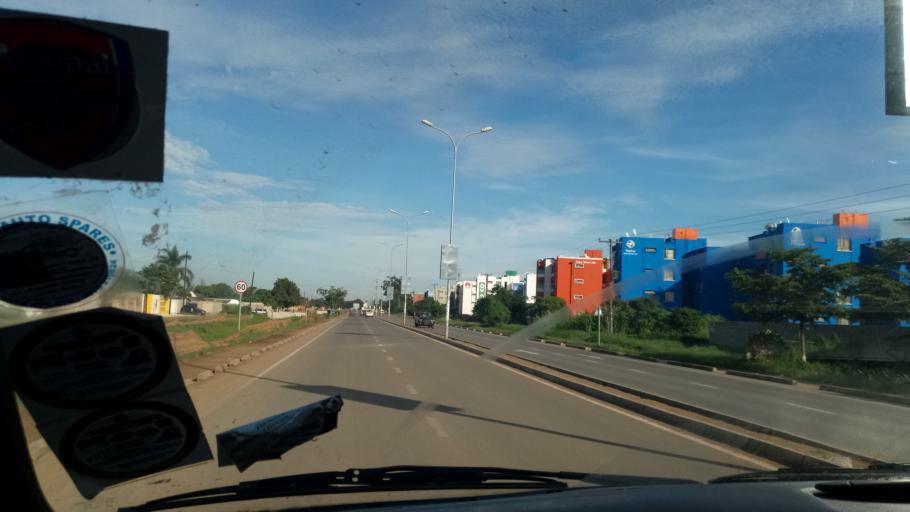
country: ZM
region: Lusaka
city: Lusaka
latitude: -15.4375
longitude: 28.3047
